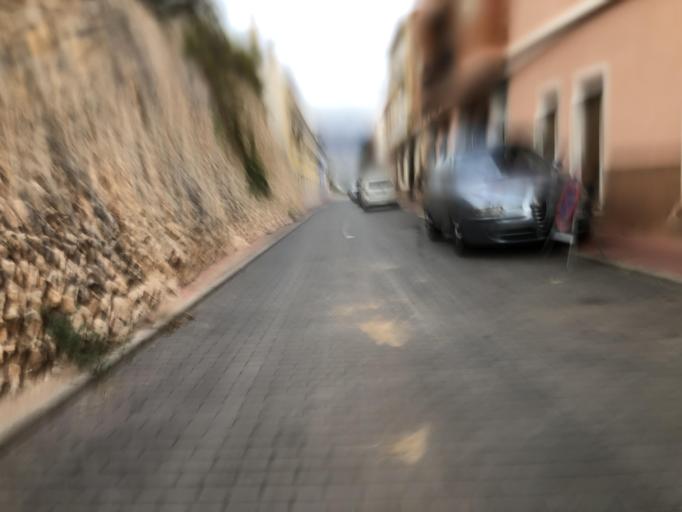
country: ES
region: Valencia
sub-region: Provincia de Alicante
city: Polop
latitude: 38.6341
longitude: -0.1351
